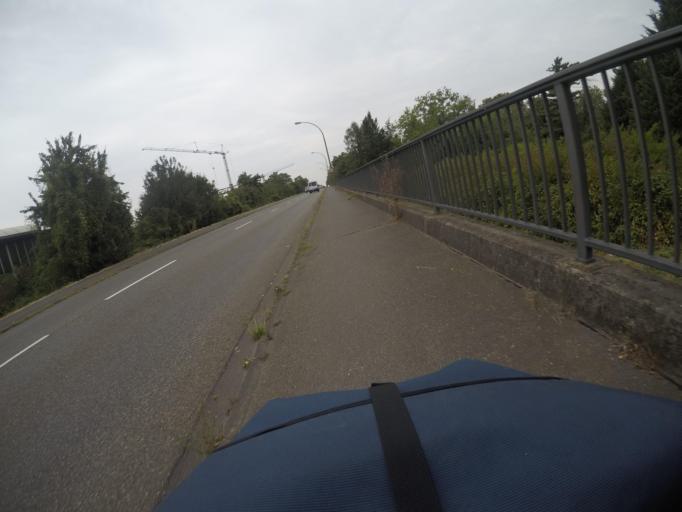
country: DE
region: North Rhine-Westphalia
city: Wesseling
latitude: 50.8167
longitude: 6.9940
